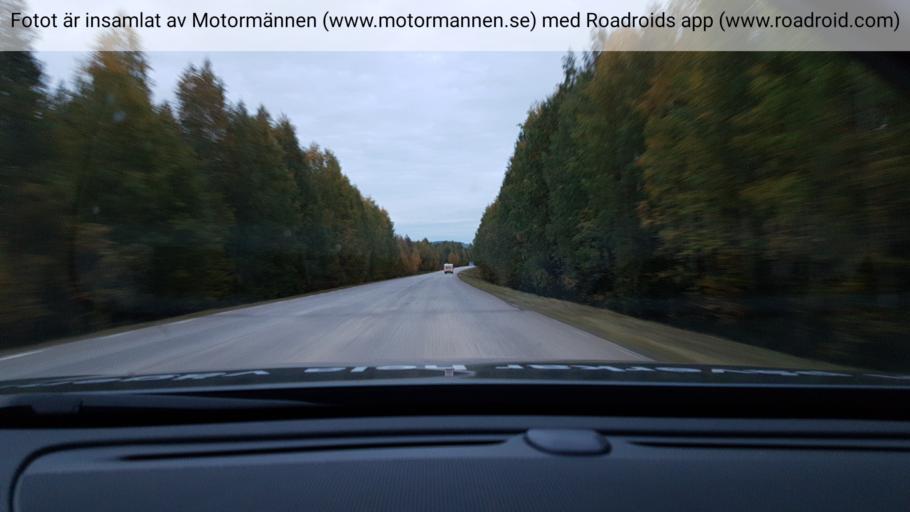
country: SE
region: Norrbotten
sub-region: Alvsbyns Kommun
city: AElvsbyn
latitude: 65.8437
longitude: 20.4913
